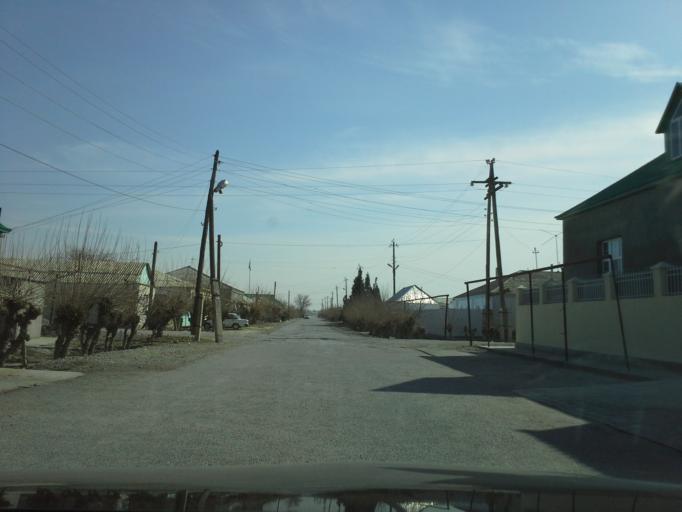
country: TM
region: Ahal
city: Abadan
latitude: 38.1087
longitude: 58.0339
